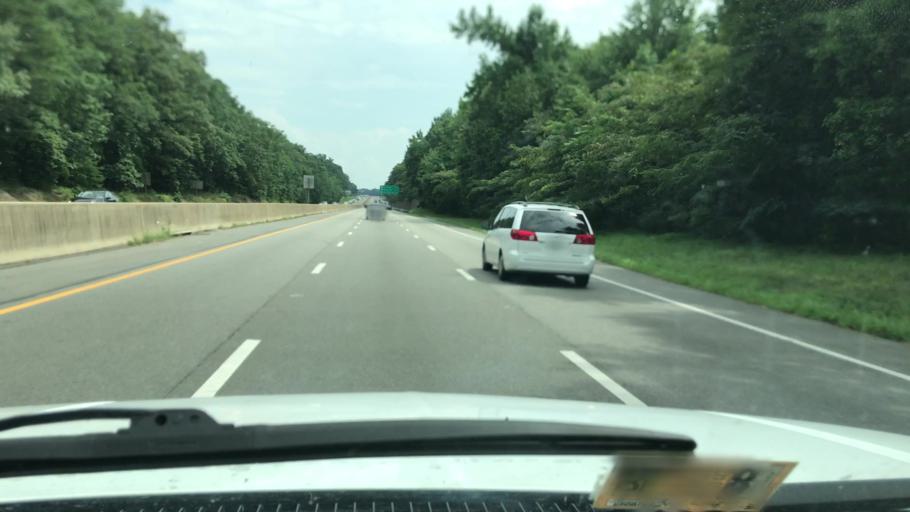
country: US
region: Virginia
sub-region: Chesterfield County
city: Bon Air
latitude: 37.4933
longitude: -77.5216
